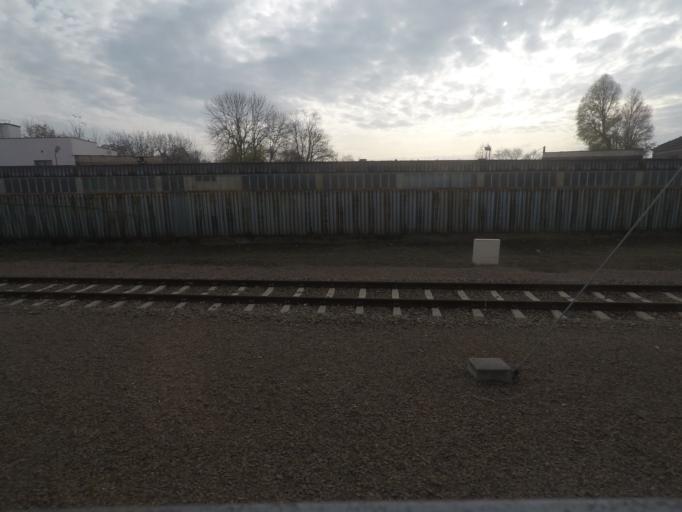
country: PL
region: Subcarpathian Voivodeship
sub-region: Powiat debicki
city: Debica
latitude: 50.0553
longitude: 21.4080
